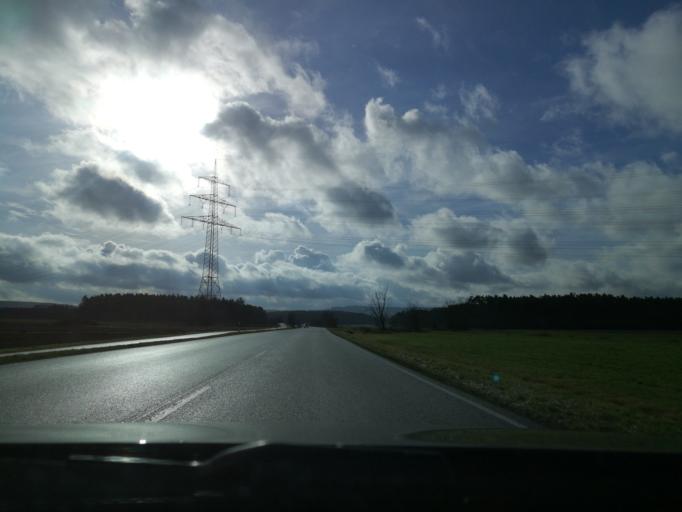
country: DE
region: Bavaria
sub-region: Regierungsbezirk Mittelfranken
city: Abenberg
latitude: 49.2380
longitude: 10.8958
